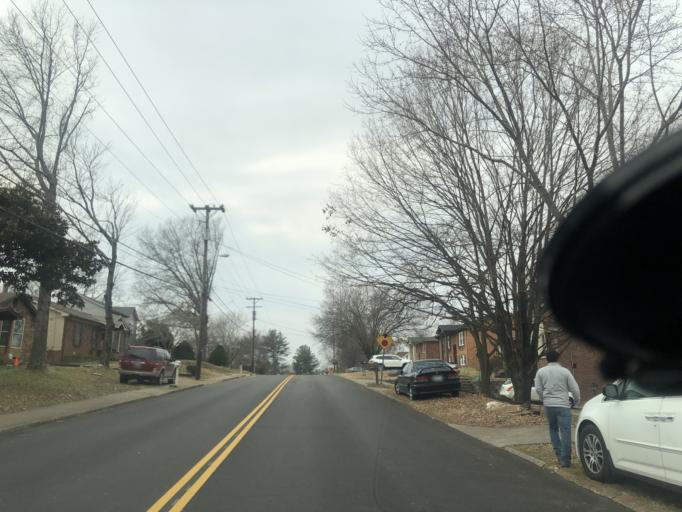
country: US
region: Tennessee
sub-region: Davidson County
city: Oak Hill
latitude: 36.0876
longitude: -86.7132
